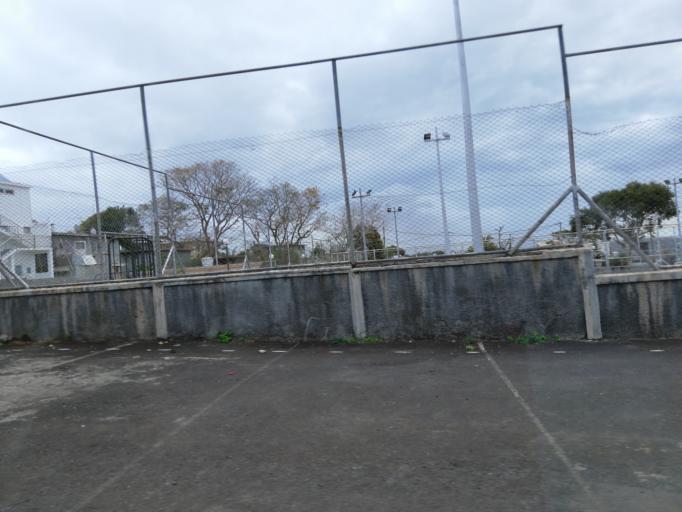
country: MU
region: Black River
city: Petite Riviere
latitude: -20.2114
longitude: 57.4652
